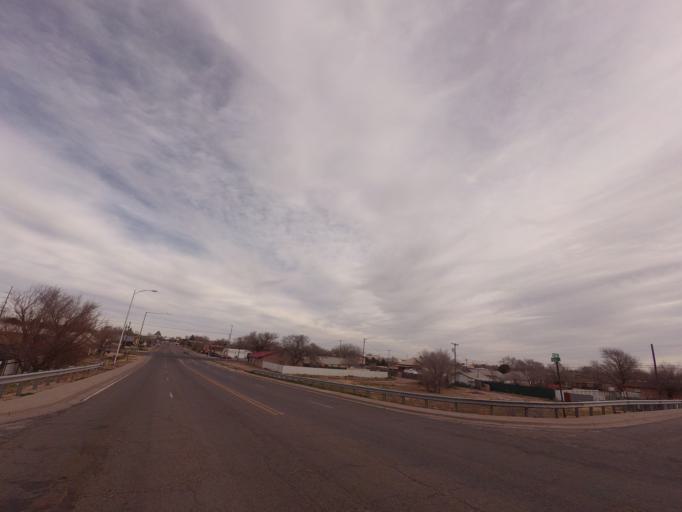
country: US
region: New Mexico
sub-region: Curry County
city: Clovis
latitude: 34.3996
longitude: -103.2205
